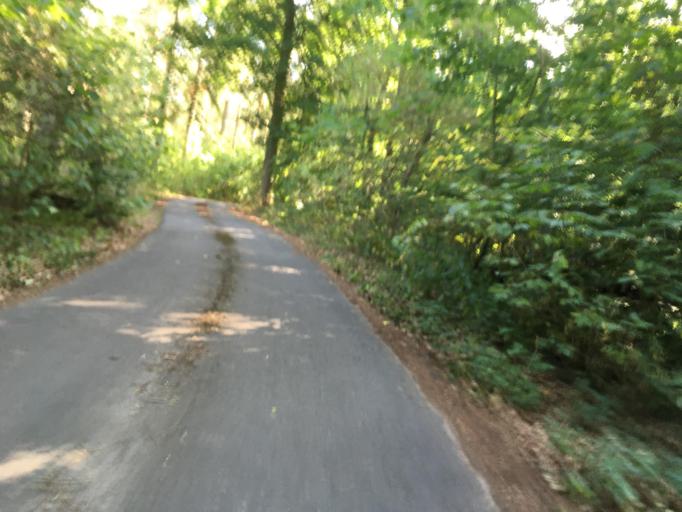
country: DE
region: Brandenburg
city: Liebenwalde
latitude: 52.9243
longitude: 13.4409
